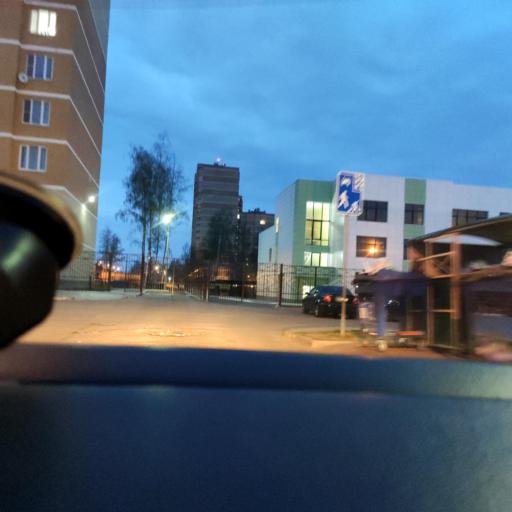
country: RU
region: Moskovskaya
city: Ramenskoye
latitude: 55.5713
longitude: 38.2572
